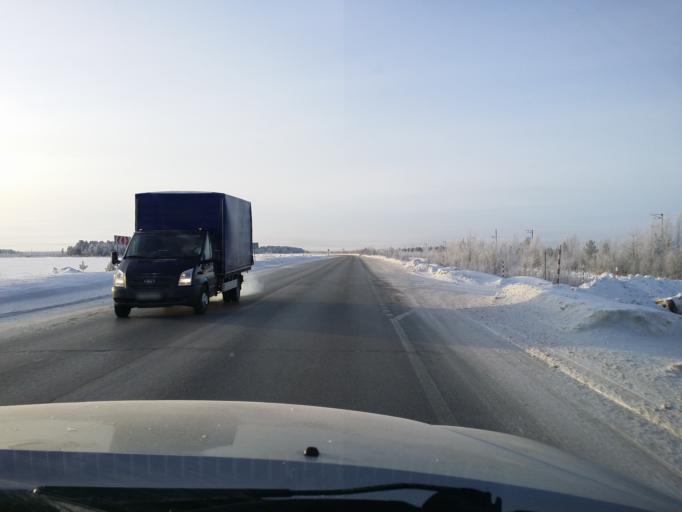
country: RU
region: Khanty-Mansiyskiy Avtonomnyy Okrug
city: Surgut
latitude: 61.4153
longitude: 73.8239
